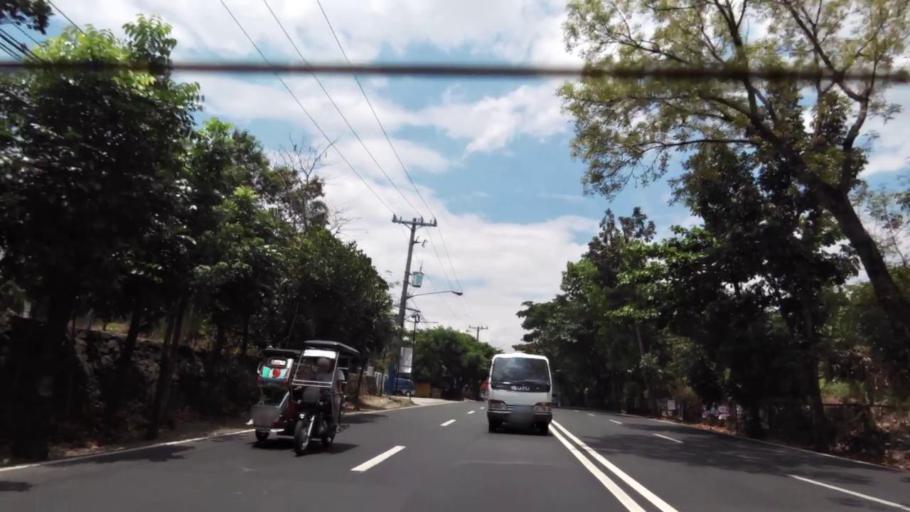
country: PH
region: Calabarzon
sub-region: Province of Rizal
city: Antipolo
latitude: 14.6115
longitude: 121.1580
